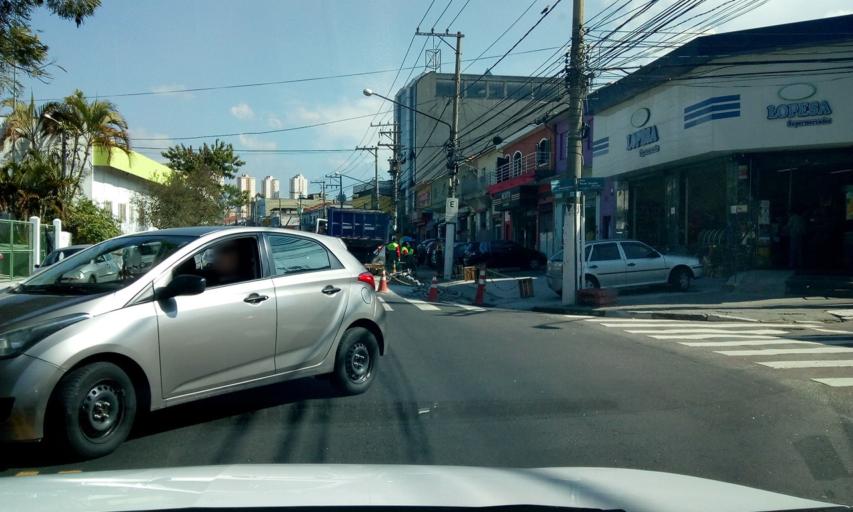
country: BR
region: Sao Paulo
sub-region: Osasco
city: Osasco
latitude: -23.5478
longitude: -46.7761
